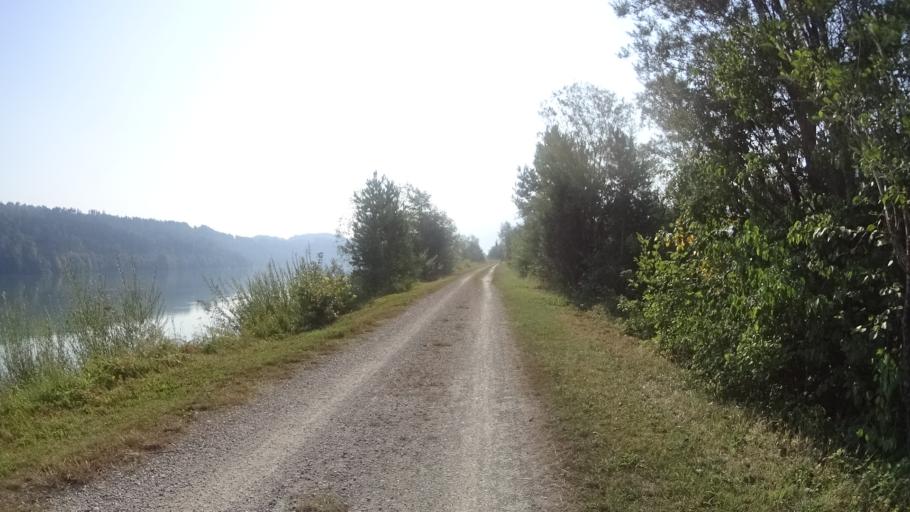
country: AT
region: Carinthia
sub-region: Politischer Bezirk Klagenfurt Land
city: Kottmannsdorf
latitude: 46.5447
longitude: 14.2231
